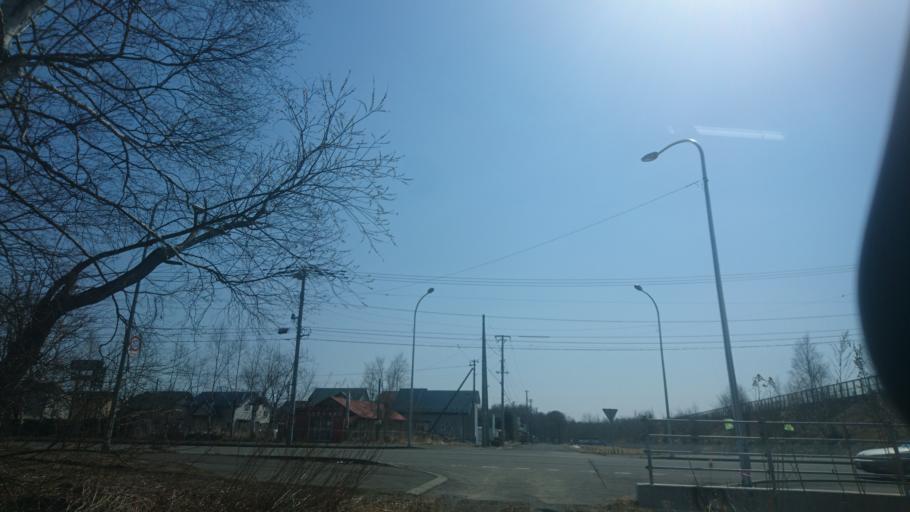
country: JP
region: Hokkaido
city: Obihiro
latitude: 42.9156
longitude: 143.1106
